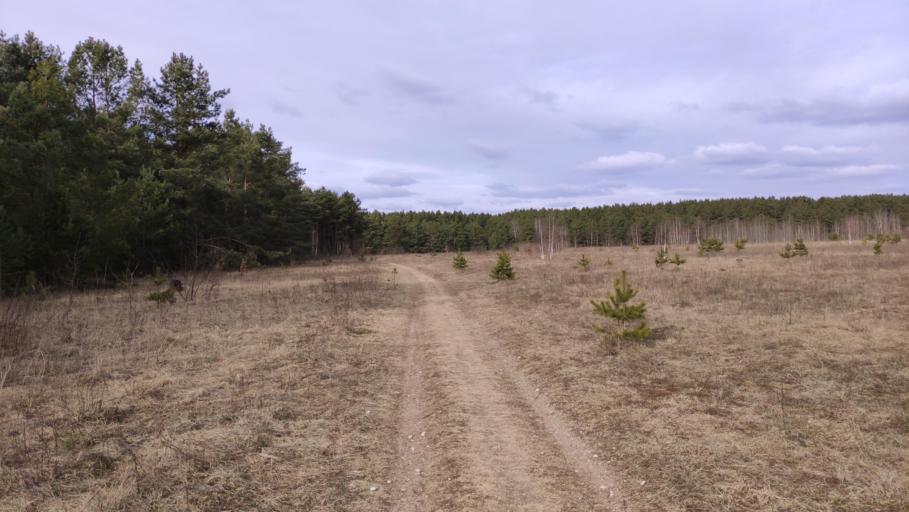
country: LT
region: Alytaus apskritis
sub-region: Alytus
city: Alytus
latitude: 54.4164
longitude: 24.0484
